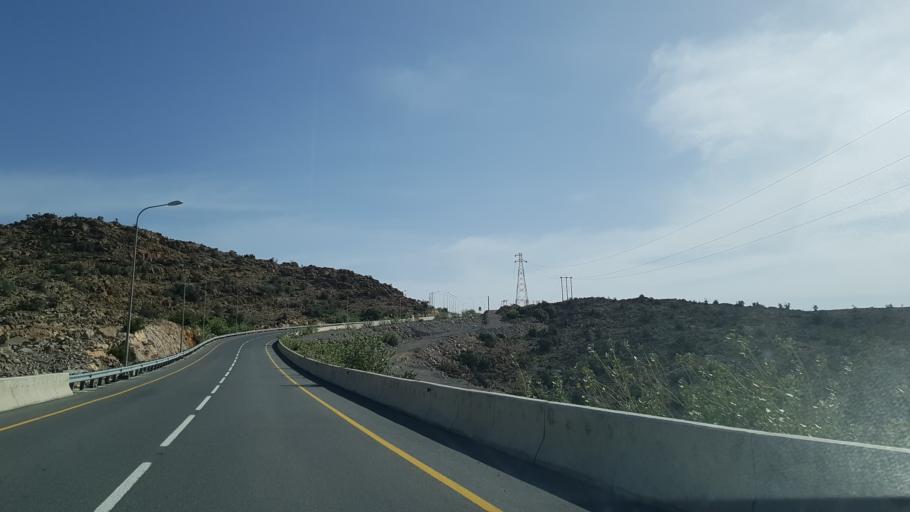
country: OM
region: Muhafazat ad Dakhiliyah
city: Izki
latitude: 23.0337
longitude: 57.7050
